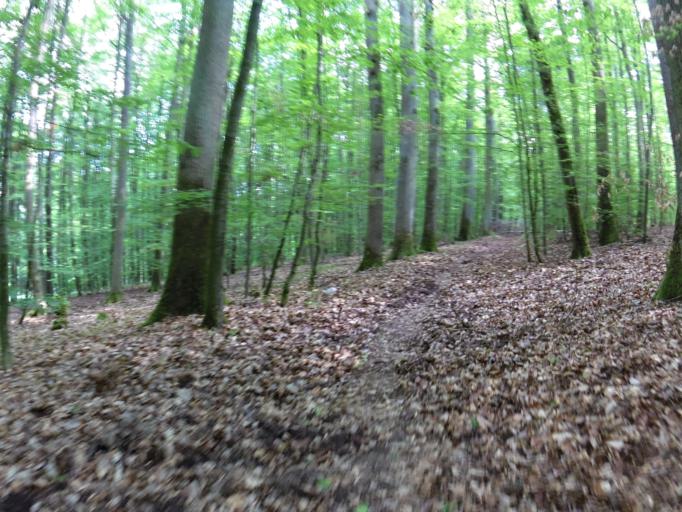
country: DE
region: Bavaria
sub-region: Regierungsbezirk Unterfranken
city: Wuerzburg
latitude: 49.7404
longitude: 9.8783
